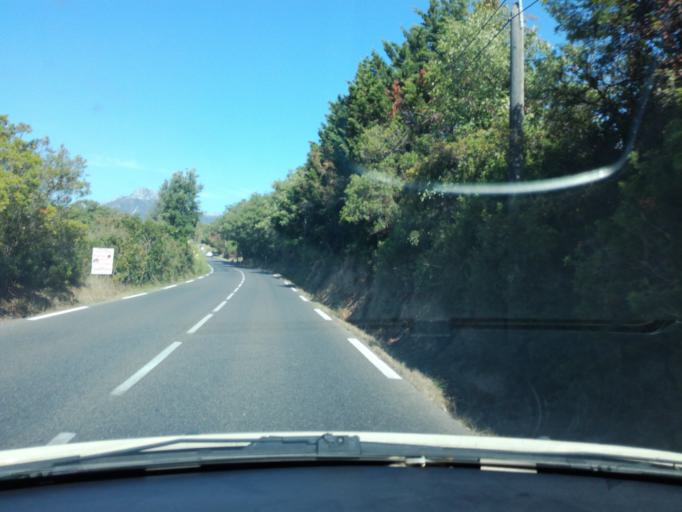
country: FR
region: Provence-Alpes-Cote d'Azur
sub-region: Departement du Var
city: La Crau
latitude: 43.1328
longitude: 6.0841
